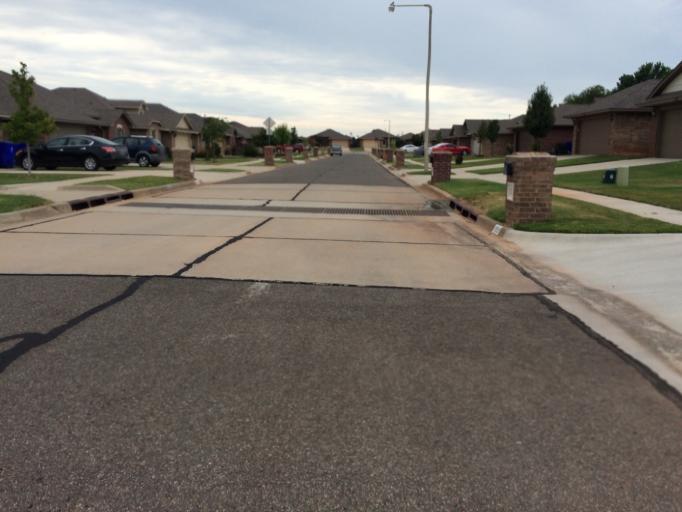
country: US
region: Oklahoma
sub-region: Cleveland County
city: Hall Park
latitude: 35.2499
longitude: -97.4172
